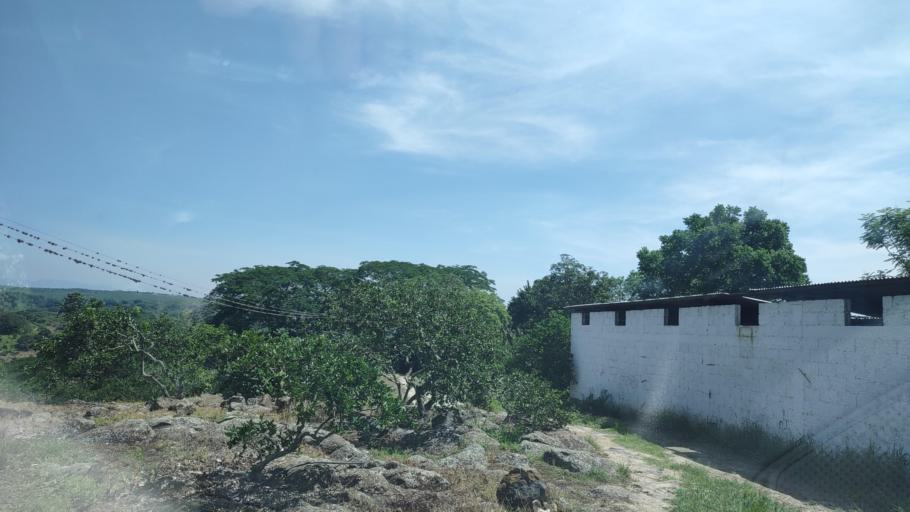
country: MX
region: Veracruz
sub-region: Emiliano Zapata
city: Dos Rios
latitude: 19.4292
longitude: -96.7938
